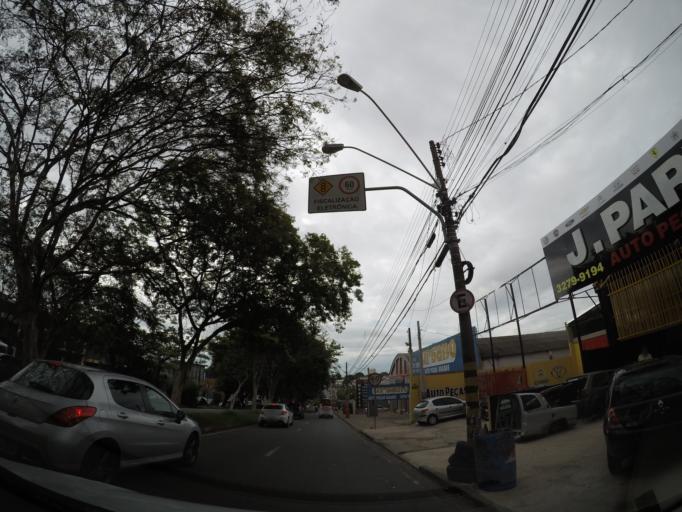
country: BR
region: Sao Paulo
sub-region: Campinas
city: Campinas
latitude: -22.9328
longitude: -47.0402
